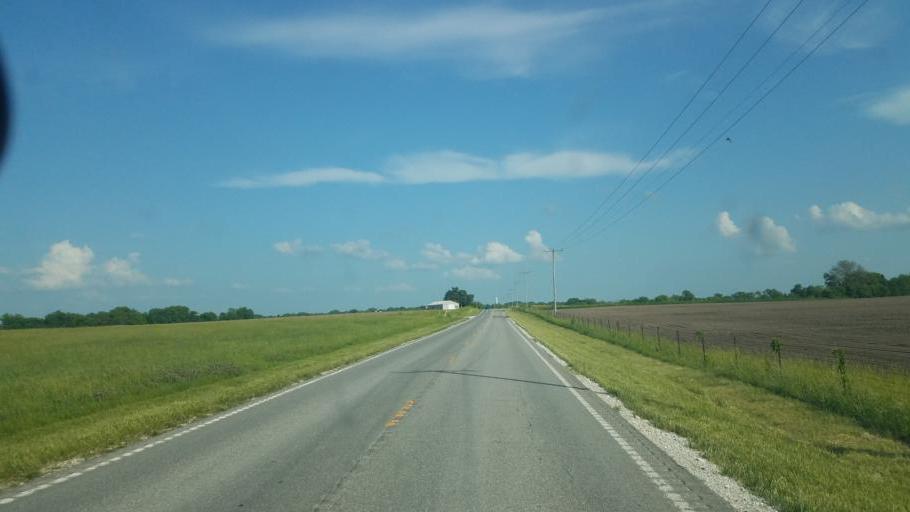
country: US
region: Missouri
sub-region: Moniteau County
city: California
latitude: 38.8249
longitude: -92.6058
